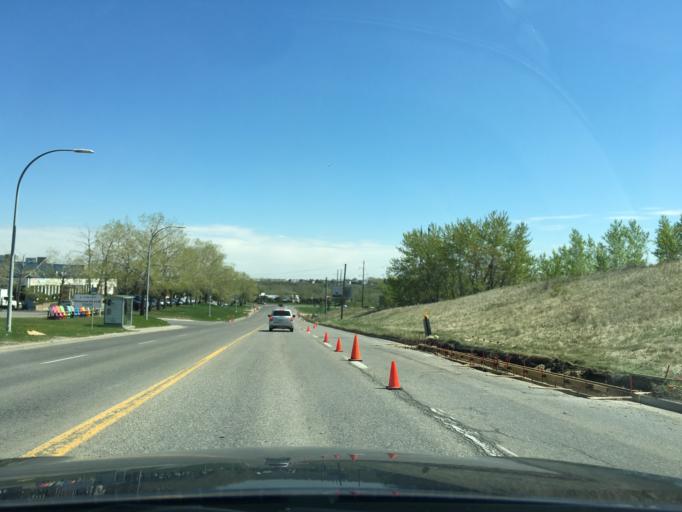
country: CA
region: Alberta
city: Calgary
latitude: 51.0017
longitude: -114.0419
